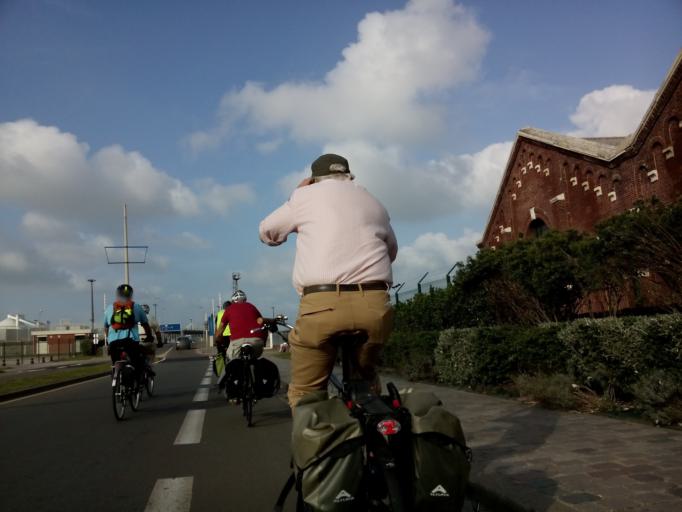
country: FR
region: Nord-Pas-de-Calais
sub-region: Departement du Pas-de-Calais
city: Calais
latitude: 50.9622
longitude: 1.8569
